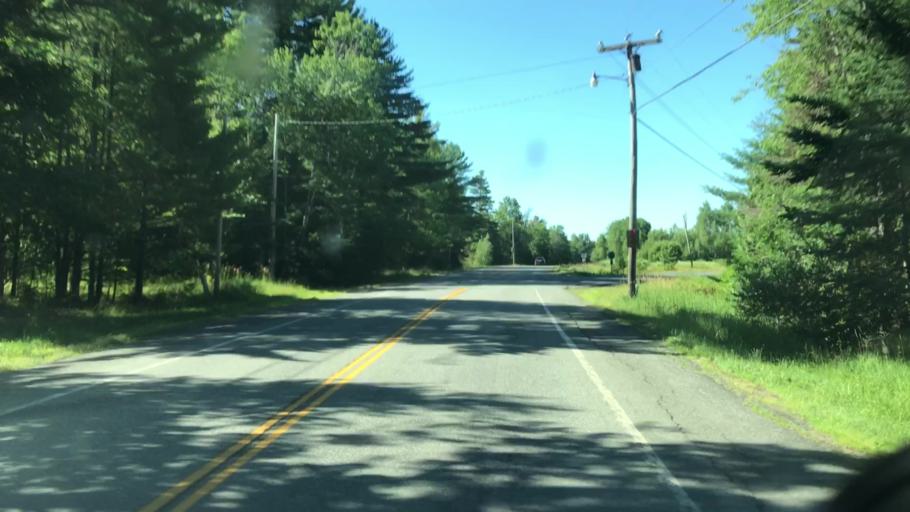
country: US
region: Maine
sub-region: Penobscot County
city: Howland
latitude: 45.2529
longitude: -68.6377
